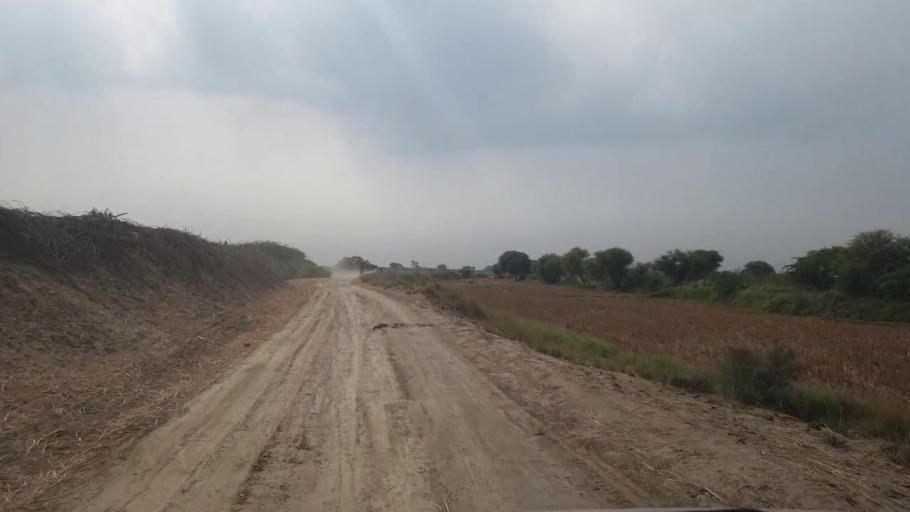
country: PK
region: Sindh
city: Talhar
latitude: 24.9291
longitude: 68.7870
